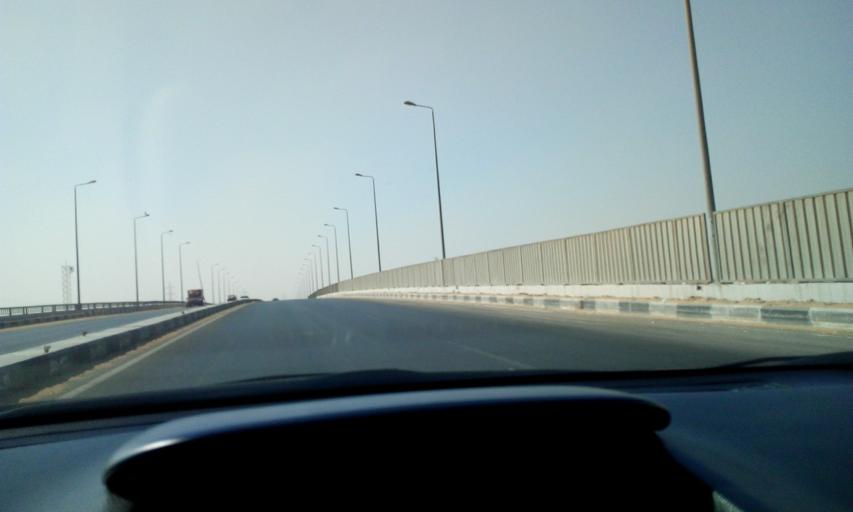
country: EG
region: Al Jizah
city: Madinat Sittah Uktubar
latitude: 29.8767
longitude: 31.0761
